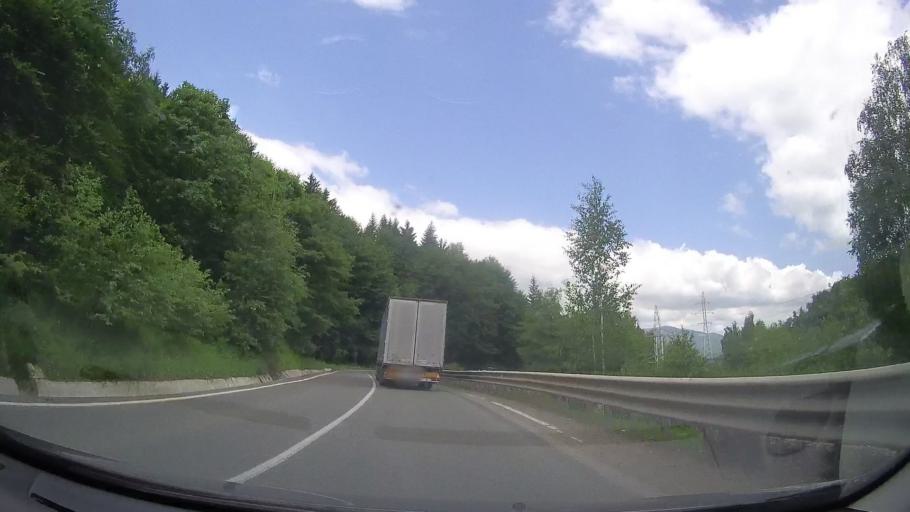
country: RO
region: Prahova
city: Maneciu
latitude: 45.3394
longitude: 25.9578
